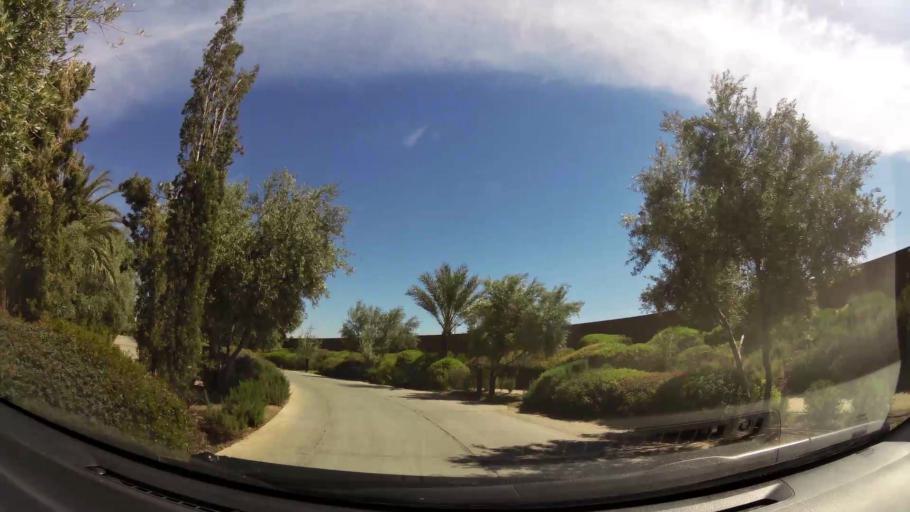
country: MA
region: Marrakech-Tensift-Al Haouz
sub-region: Marrakech
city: Marrakesh
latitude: 31.6023
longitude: -7.9531
